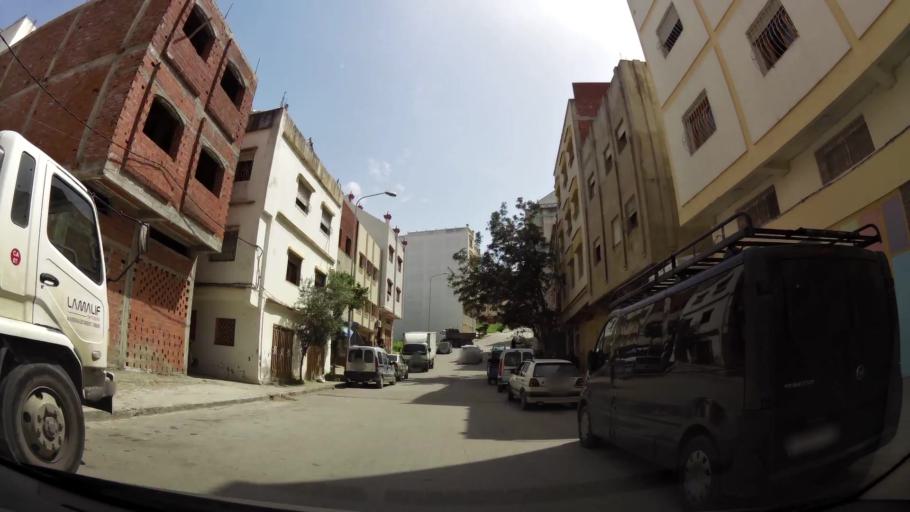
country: MA
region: Tanger-Tetouan
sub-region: Tanger-Assilah
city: Tangier
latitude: 35.7502
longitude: -5.8322
